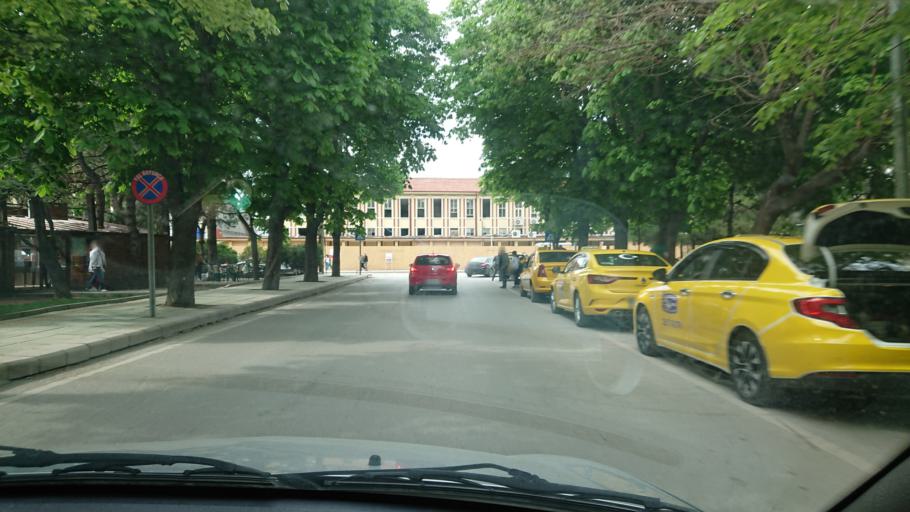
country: TR
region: Eskisehir
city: Eskisehir
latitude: 39.7789
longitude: 30.5084
